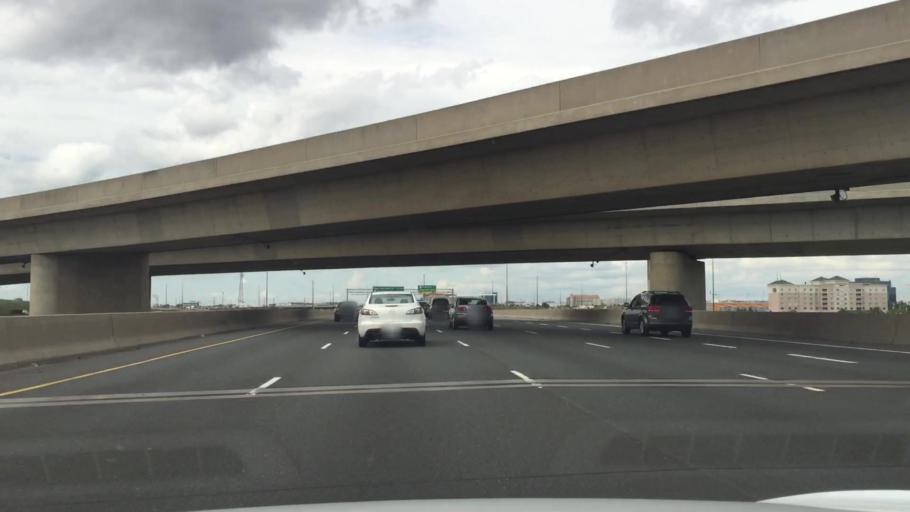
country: CA
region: Ontario
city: Concord
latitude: 43.7823
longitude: -79.5365
